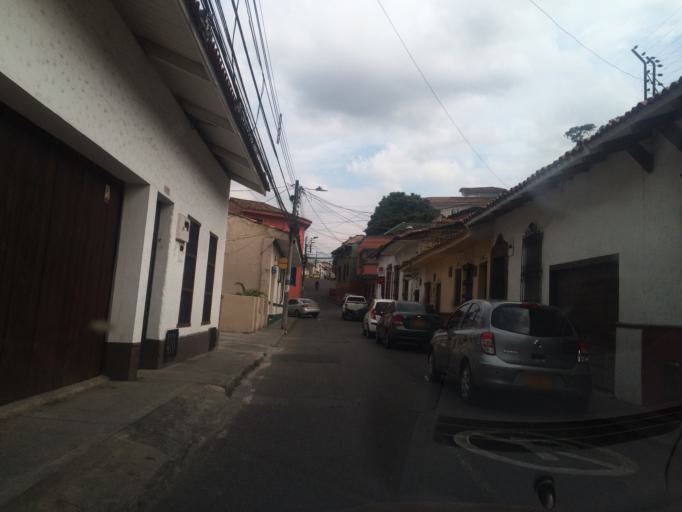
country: CO
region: Valle del Cauca
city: Cali
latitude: 3.4482
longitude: -76.5399
